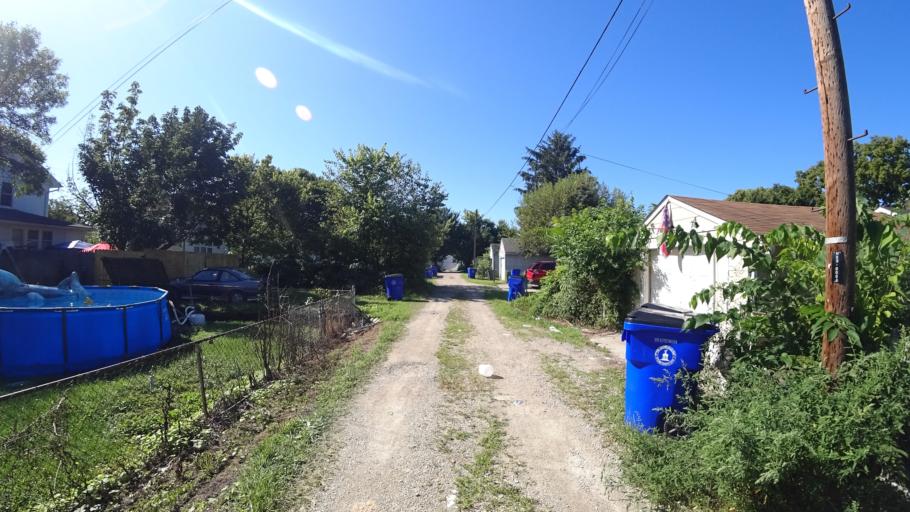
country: US
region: Ohio
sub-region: Butler County
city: Hamilton
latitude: 39.3995
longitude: -84.5426
